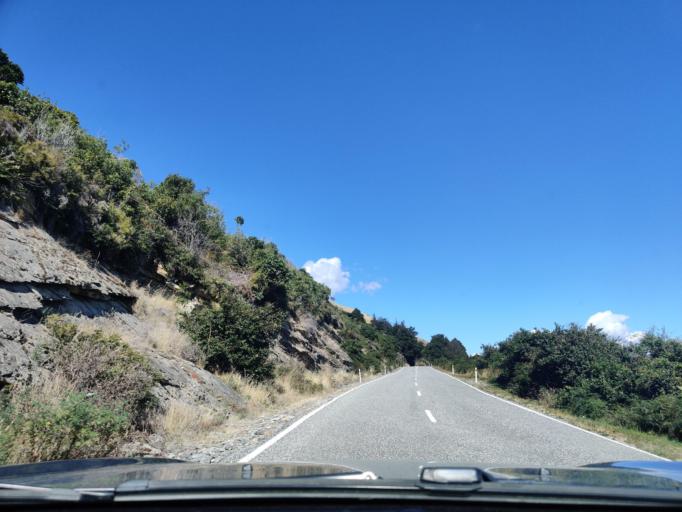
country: NZ
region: Otago
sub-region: Queenstown-Lakes District
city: Queenstown
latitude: -44.9527
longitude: 168.4372
